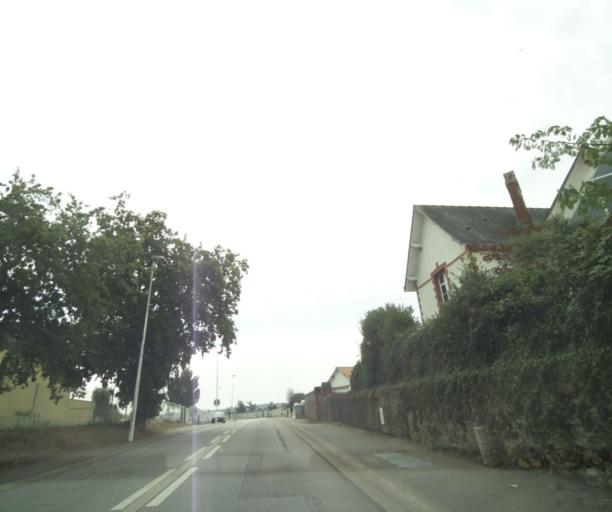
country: FR
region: Pays de la Loire
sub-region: Departement de la Loire-Atlantique
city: Saint-Herblain
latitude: 47.2057
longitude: -1.6347
